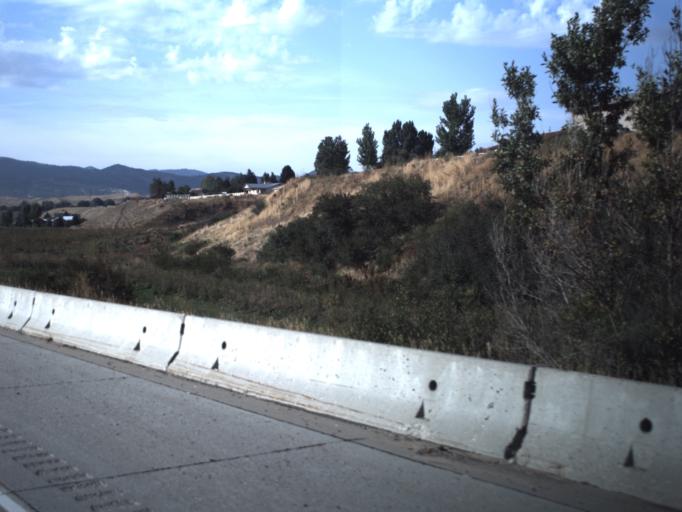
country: US
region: Utah
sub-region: Morgan County
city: Mountain Green
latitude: 41.1273
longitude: -111.7699
